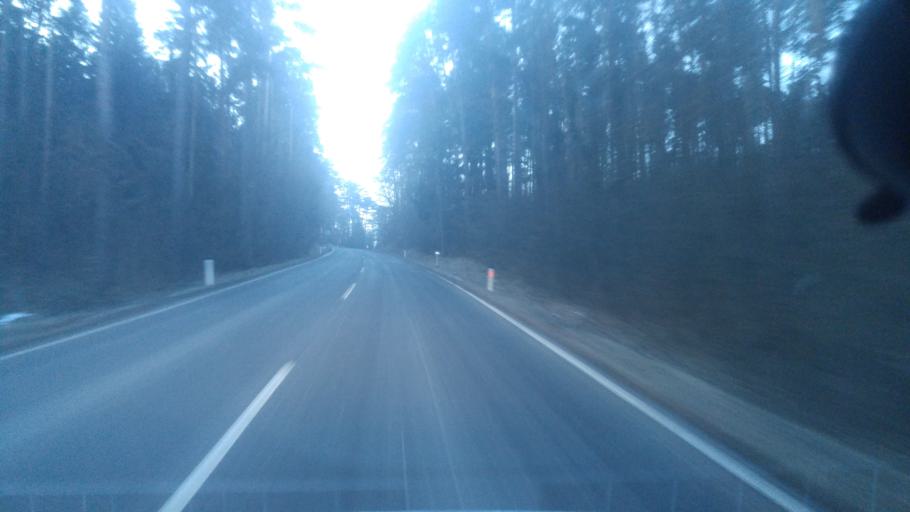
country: AT
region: Lower Austria
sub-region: Politischer Bezirk Baden
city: Berndorf
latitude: 47.9559
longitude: 16.1345
